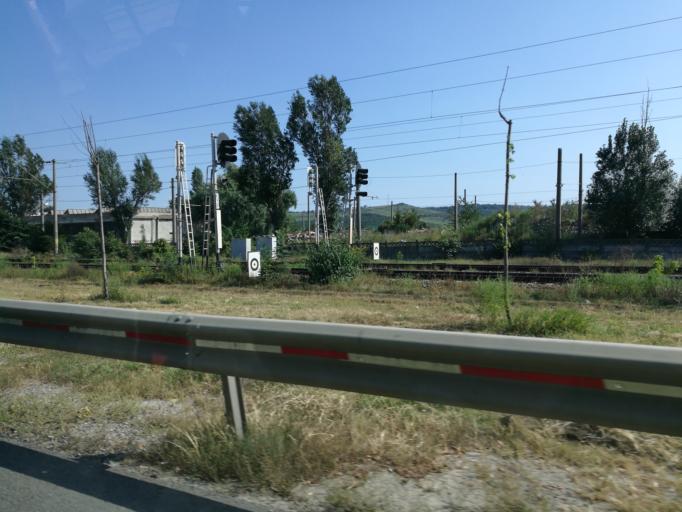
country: RO
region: Iasi
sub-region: Comuna Miroslava
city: Miroslava
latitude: 47.1722
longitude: 27.5314
